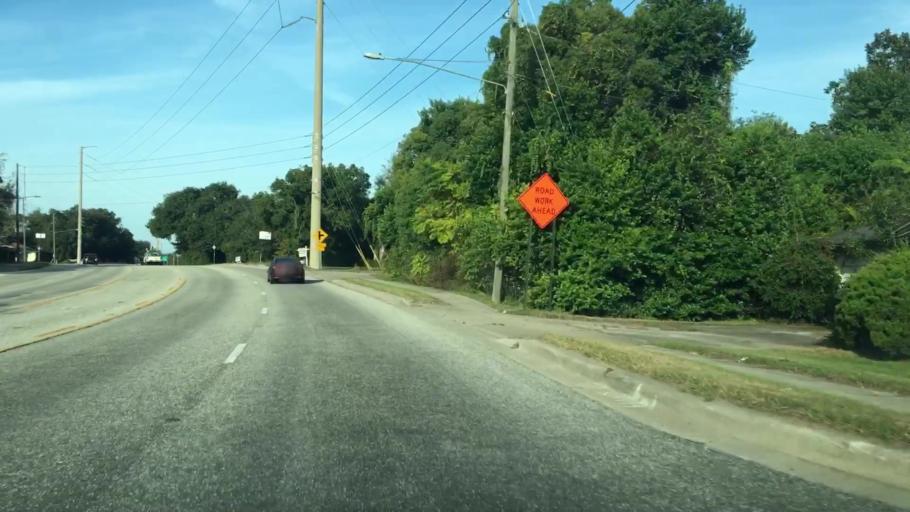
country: US
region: Florida
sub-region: Volusia County
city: Deltona
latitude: 28.9111
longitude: -81.2617
